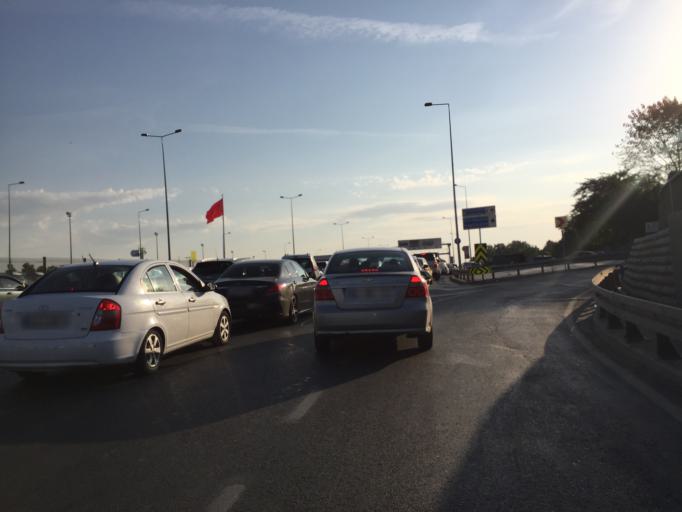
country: TR
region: Istanbul
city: Istanbul
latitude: 41.0024
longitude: 28.9509
